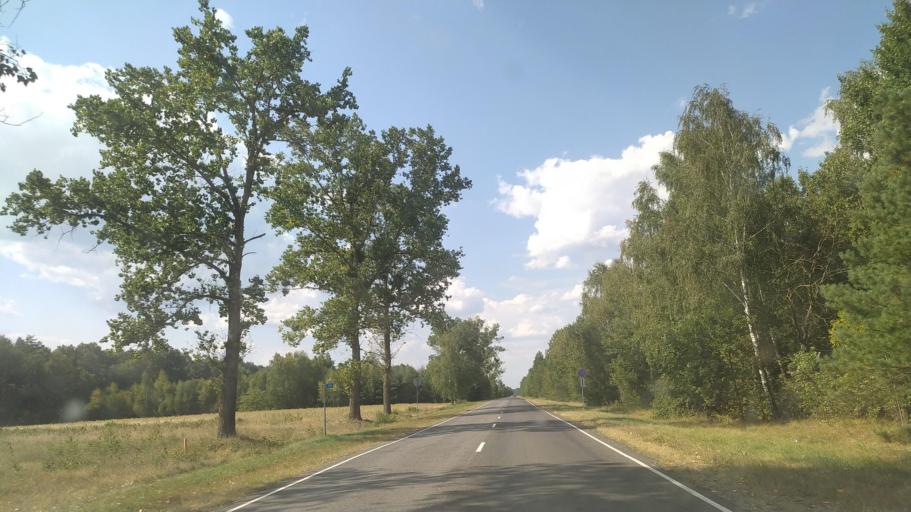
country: BY
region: Brest
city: Drahichyn
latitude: 52.2129
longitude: 25.1347
